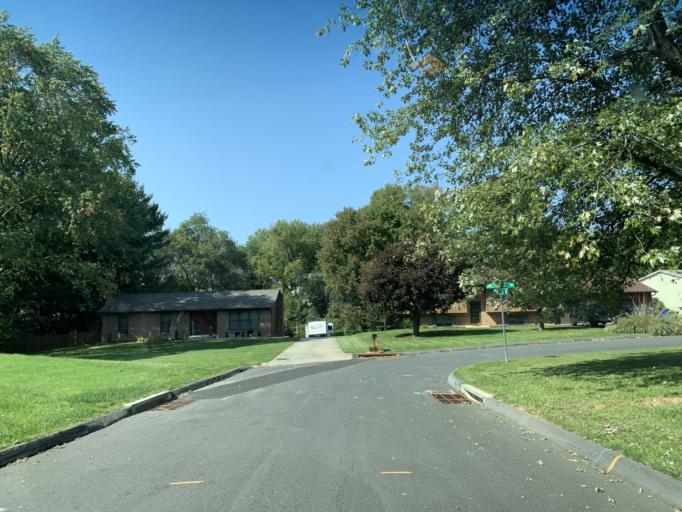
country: US
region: Maryland
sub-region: Harford County
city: South Bel Air
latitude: 39.5189
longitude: -76.3405
